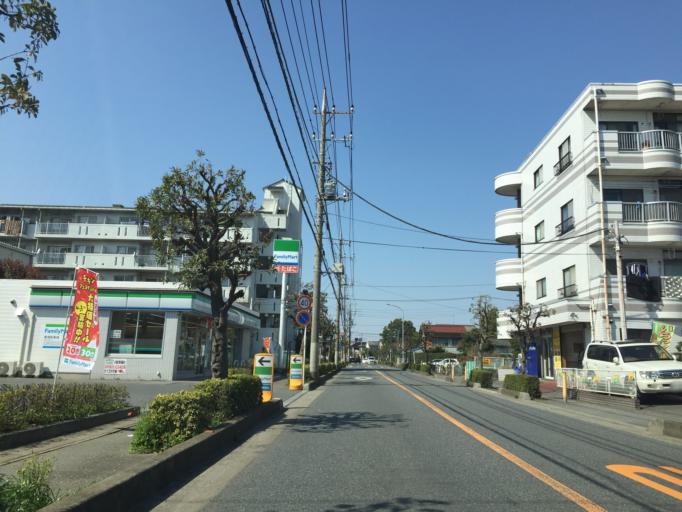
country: JP
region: Saitama
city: Shiki
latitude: 35.8433
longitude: 139.5917
